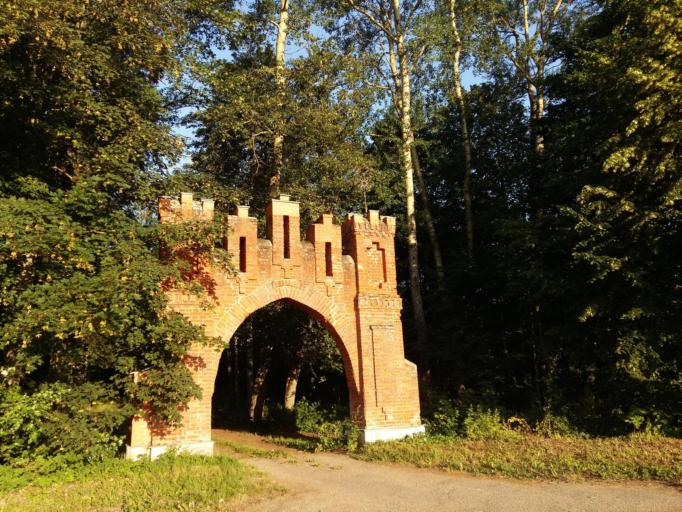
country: LT
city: Ariogala
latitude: 55.4030
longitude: 23.6400
